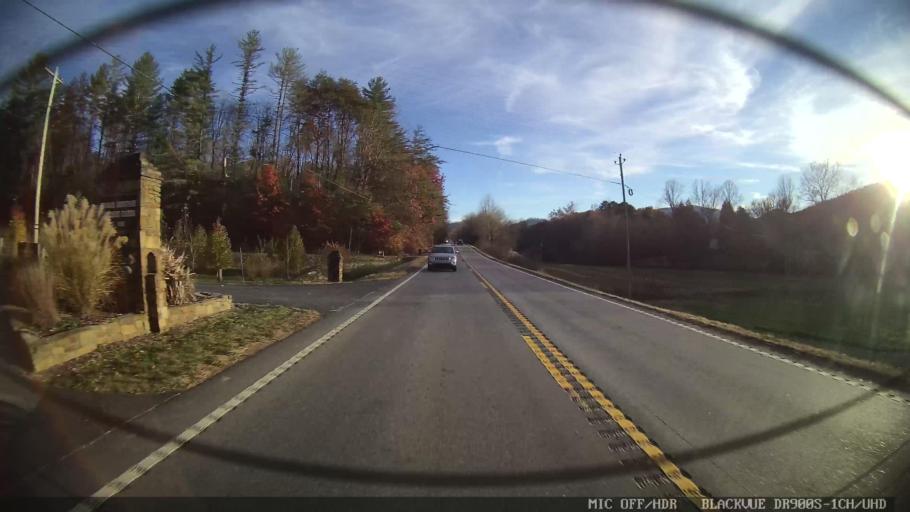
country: US
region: Georgia
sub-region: Union County
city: Blairsville
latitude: 34.8372
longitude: -83.9306
